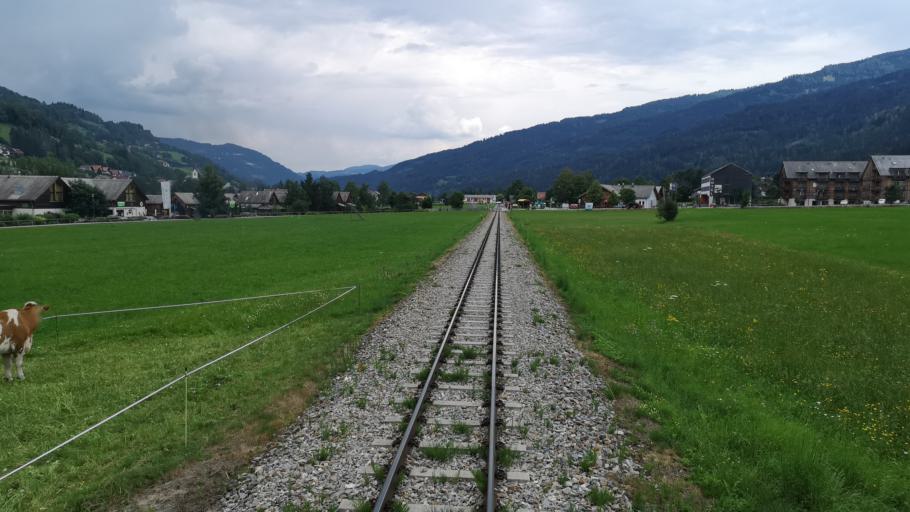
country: AT
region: Styria
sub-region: Politischer Bezirk Murau
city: Sankt Georgen ob Murau
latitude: 47.1022
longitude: 14.0846
